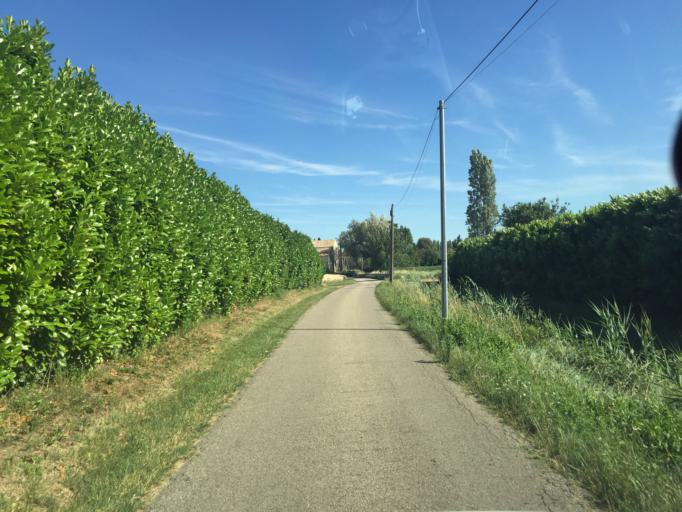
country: FR
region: Provence-Alpes-Cote d'Azur
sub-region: Departement du Vaucluse
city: Caderousse
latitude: 44.1052
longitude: 4.7420
